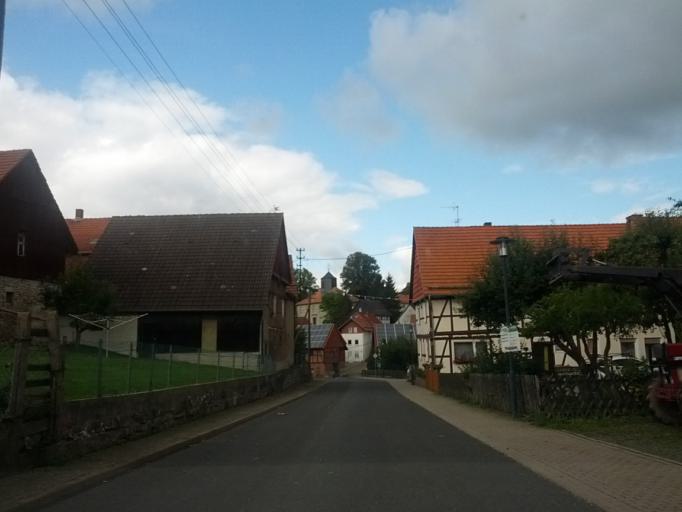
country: DE
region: Hesse
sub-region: Regierungsbezirk Kassel
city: Weissenborn
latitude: 51.0671
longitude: 10.0775
